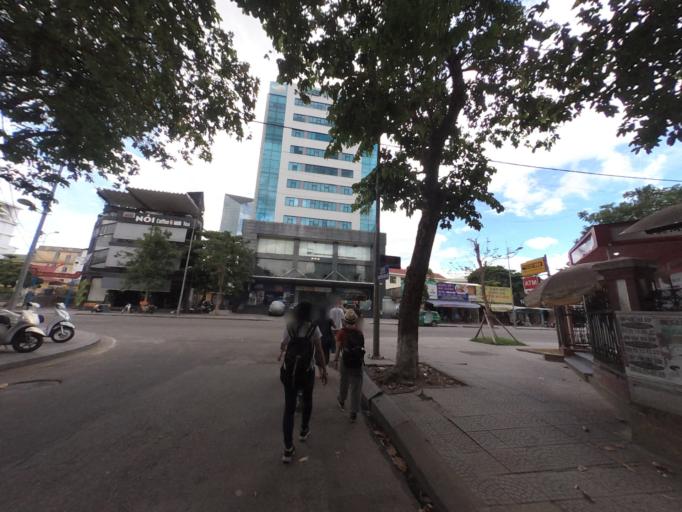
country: VN
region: Thua Thien-Hue
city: Hue
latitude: 16.4617
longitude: 107.5911
